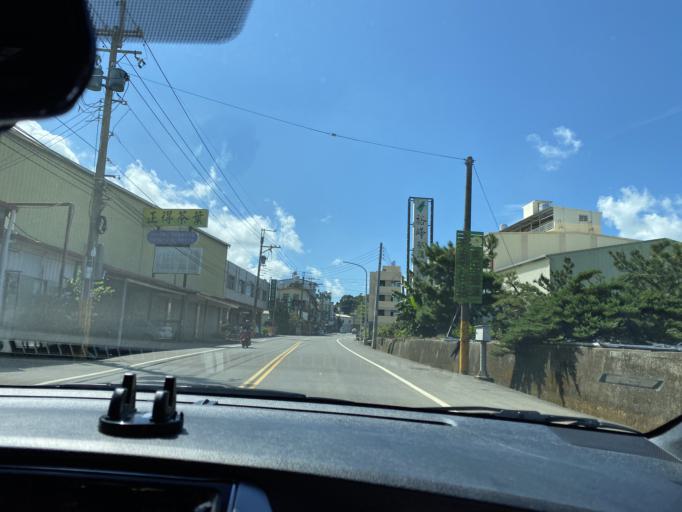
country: TW
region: Taiwan
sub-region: Nantou
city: Nantou
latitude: 23.8481
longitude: 120.6290
